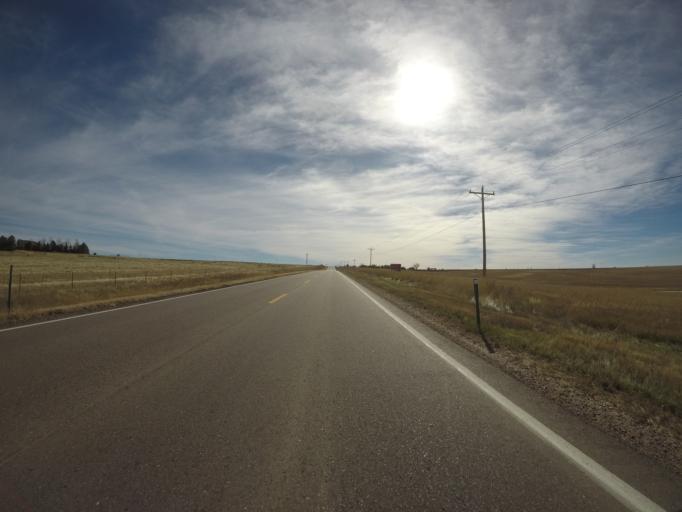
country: US
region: Colorado
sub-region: Adams County
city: Bennett
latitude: 39.7430
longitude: -104.4047
